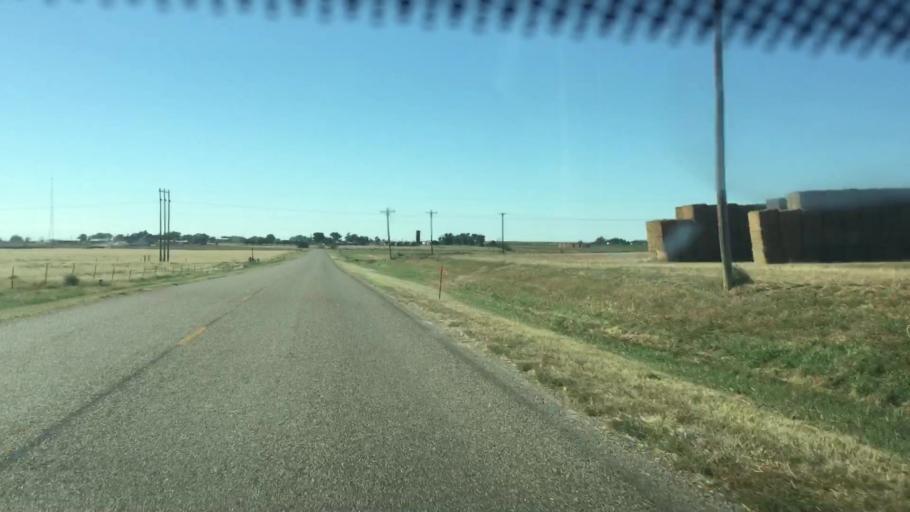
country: US
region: Colorado
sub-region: Prowers County
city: Lamar
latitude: 38.1166
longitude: -102.6024
